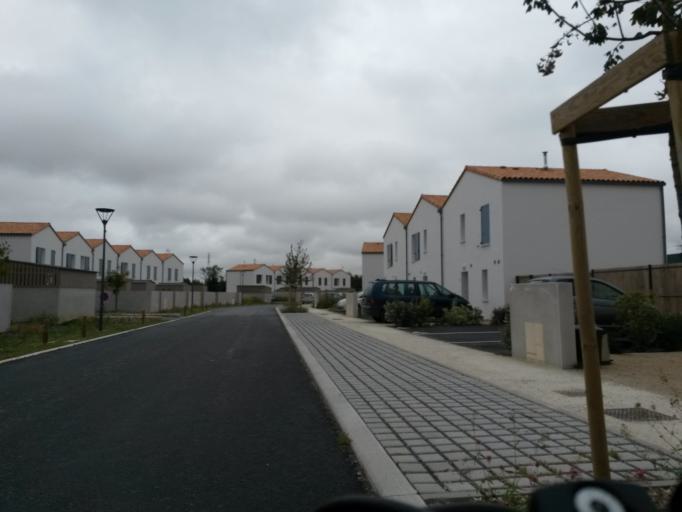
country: FR
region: Poitou-Charentes
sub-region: Departement de la Charente-Maritime
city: Saint-Xandre
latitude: 46.2071
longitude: -1.0919
